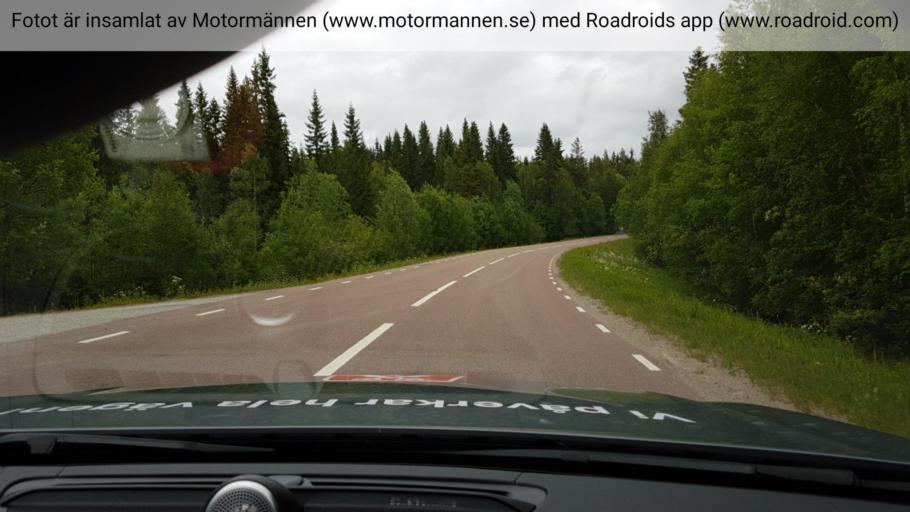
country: SE
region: Jaemtland
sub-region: Braecke Kommun
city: Braecke
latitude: 62.9602
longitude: 15.7476
